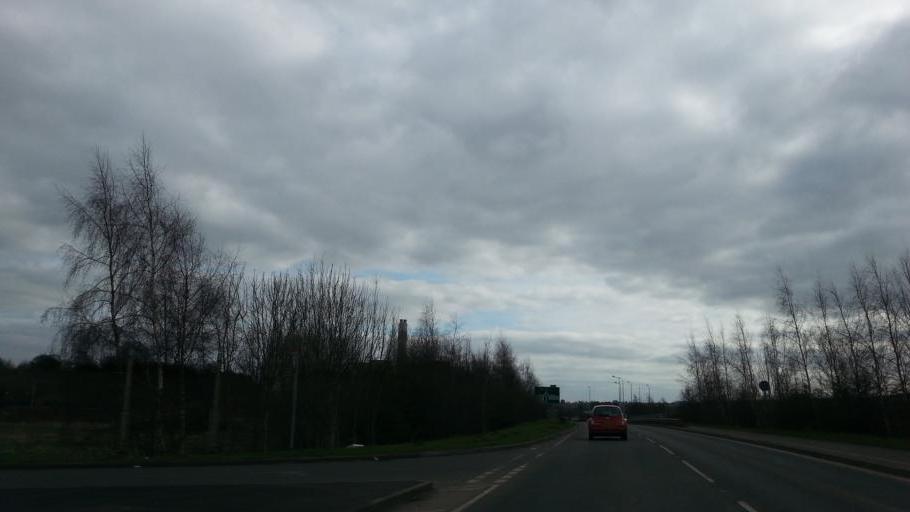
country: GB
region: England
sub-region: Staffordshire
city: Rugeley
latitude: 52.7688
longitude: -1.9324
